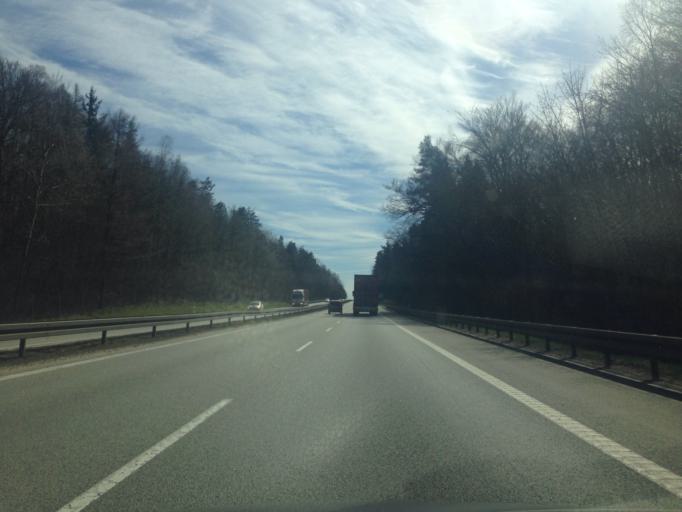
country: PL
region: Pomeranian Voivodeship
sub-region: Gdynia
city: Wielki Kack
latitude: 54.4461
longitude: 18.4912
